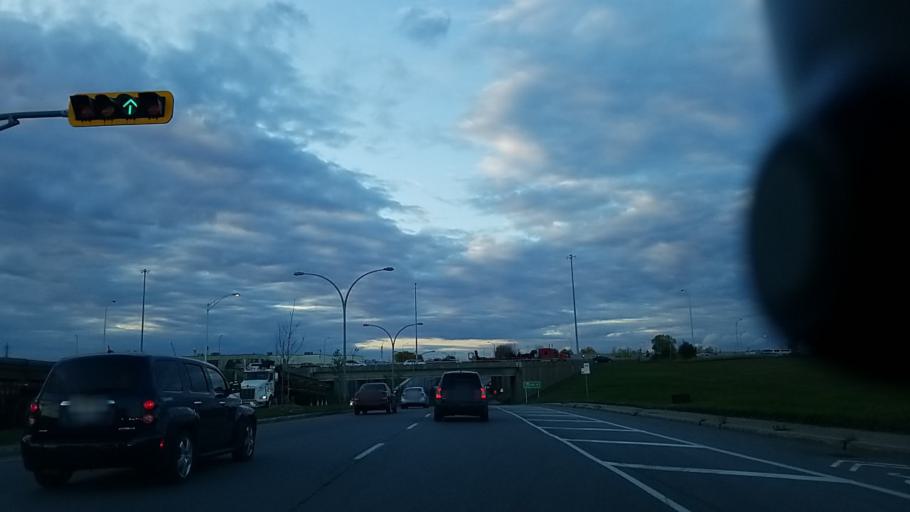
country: CA
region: Quebec
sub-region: Laval
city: Laval
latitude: 45.5838
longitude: -73.7346
